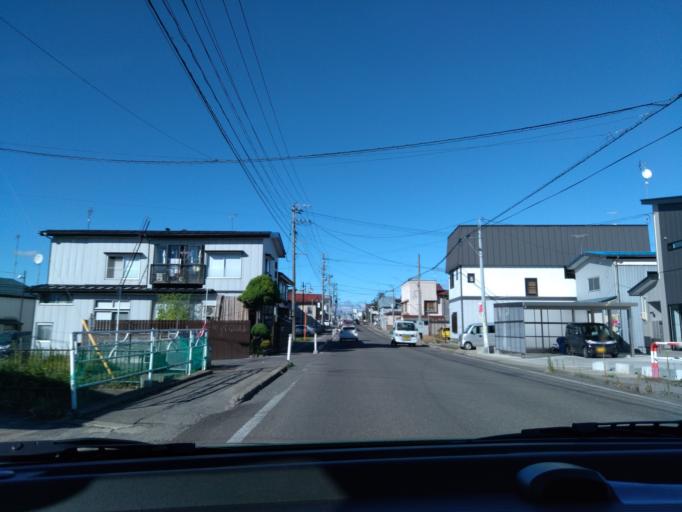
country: JP
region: Akita
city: Yuzawa
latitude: 39.2204
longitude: 140.5211
